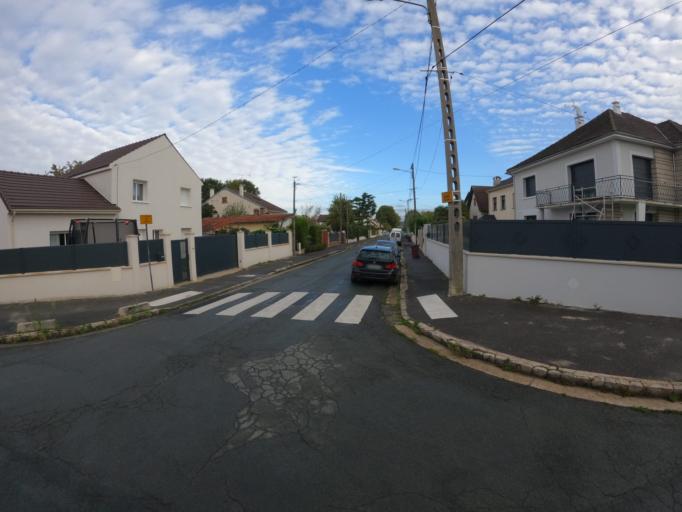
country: FR
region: Ile-de-France
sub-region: Departement de Seine-Saint-Denis
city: Montfermeil
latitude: 48.8999
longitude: 2.5956
